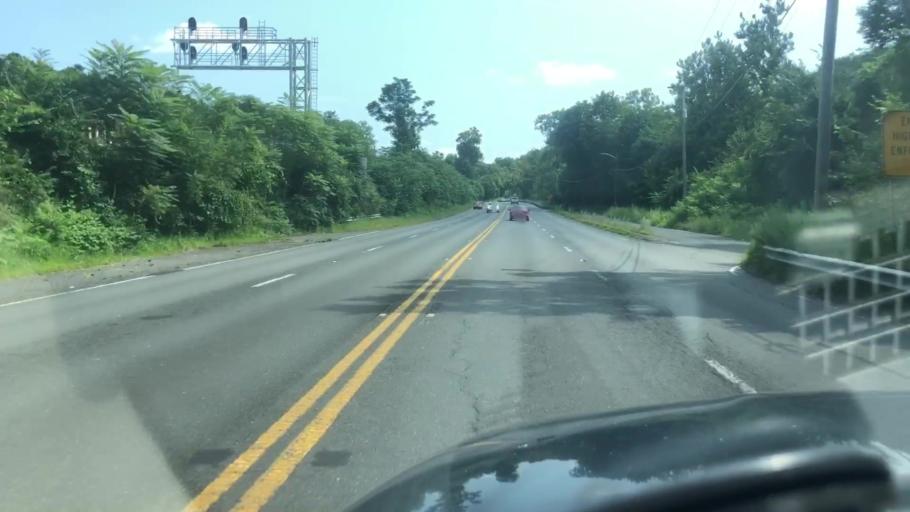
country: US
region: Massachusetts
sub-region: Hampden County
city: Westfield
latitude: 42.1068
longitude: -72.6986
